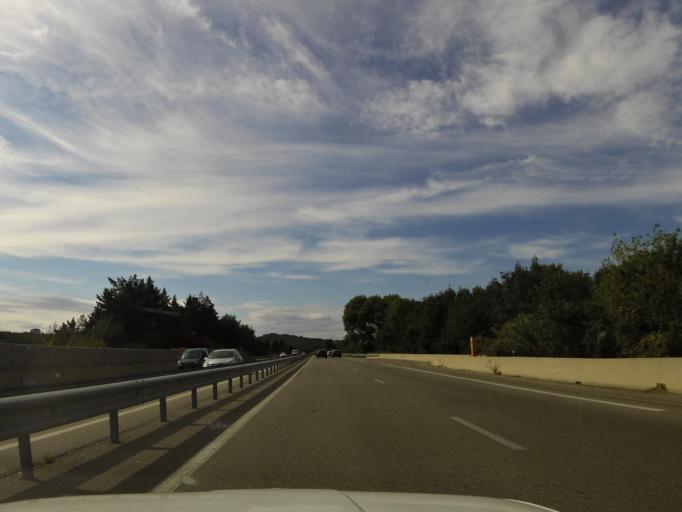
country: FR
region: Languedoc-Roussillon
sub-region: Departement du Gard
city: Moussac
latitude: 43.9985
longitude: 4.1851
